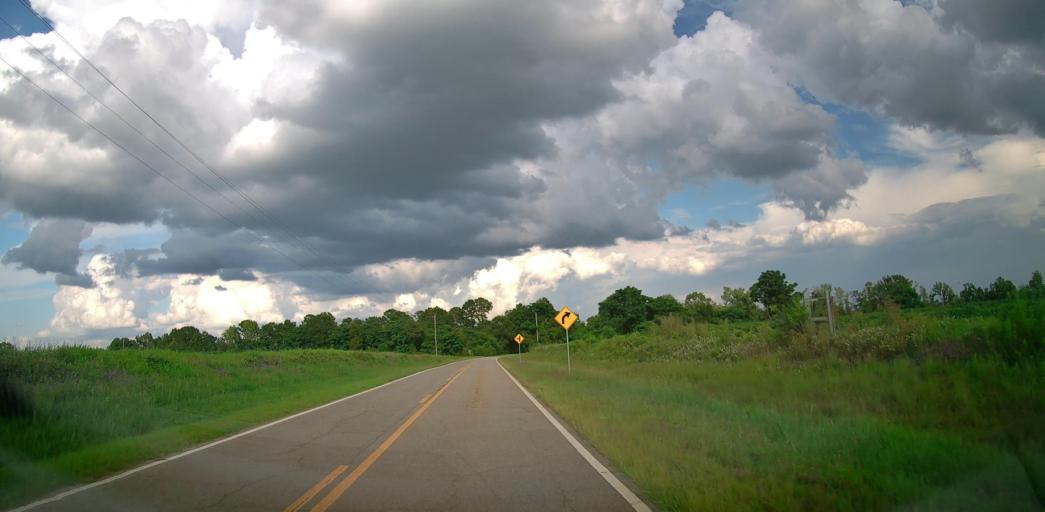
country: US
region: Georgia
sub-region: Bleckley County
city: Cochran
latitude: 32.4100
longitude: -83.3913
